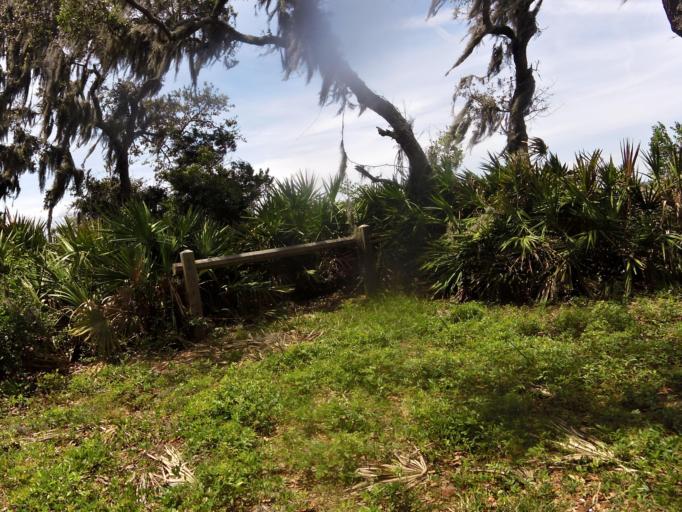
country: US
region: Florida
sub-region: Nassau County
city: Fernandina Beach
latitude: 30.5011
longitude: -81.4942
